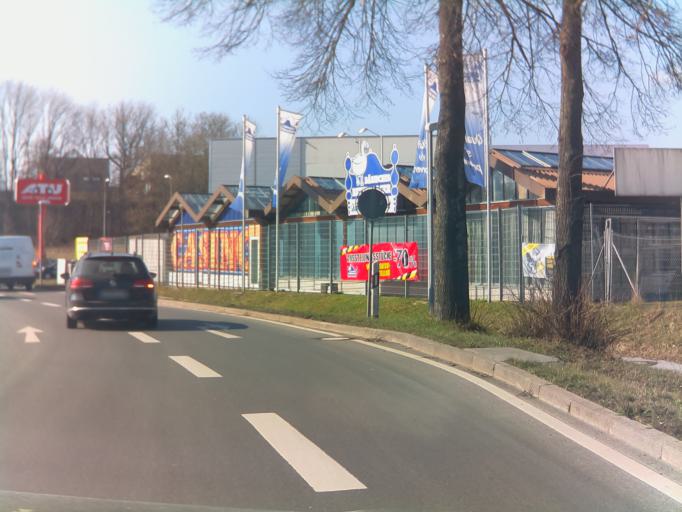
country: DE
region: Baden-Wuerttemberg
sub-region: Karlsruhe Region
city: Horb am Neckar
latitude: 48.4565
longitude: 8.7008
